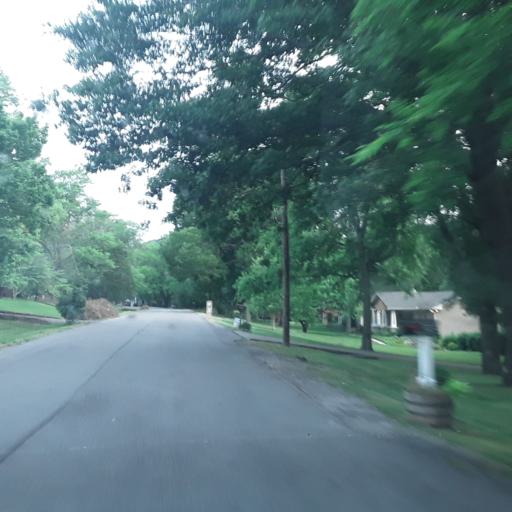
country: US
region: Tennessee
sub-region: Williamson County
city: Brentwood
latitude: 36.0581
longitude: -86.7657
